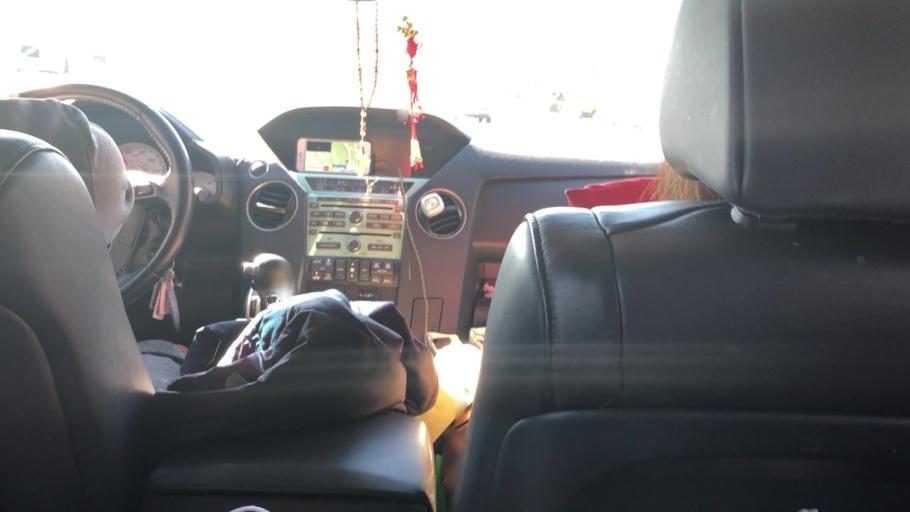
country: US
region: Louisiana
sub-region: Saint John the Baptist Parish
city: Montegut
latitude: 30.1009
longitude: -90.5052
